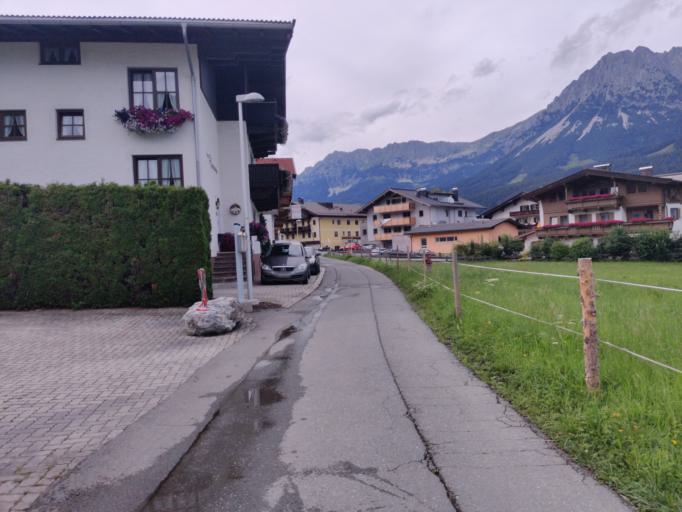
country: AT
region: Tyrol
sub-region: Politischer Bezirk Kufstein
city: Ellmau
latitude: 47.5126
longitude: 12.3057
